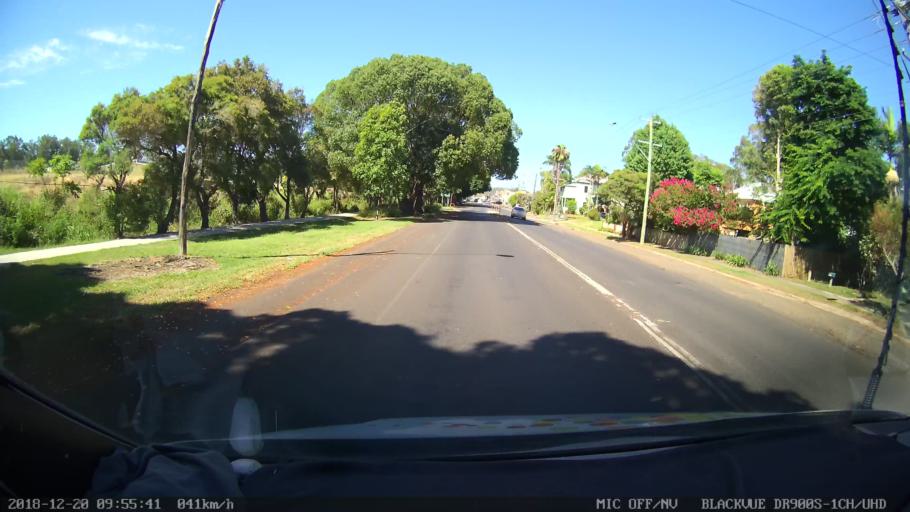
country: AU
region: New South Wales
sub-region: Lismore Municipality
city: Lismore
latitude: -28.8074
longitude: 153.2722
